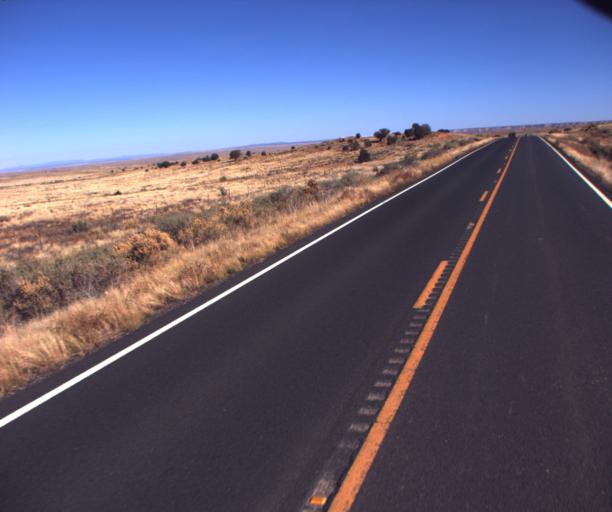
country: US
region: Arizona
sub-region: Apache County
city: Ganado
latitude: 35.7849
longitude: -109.7051
